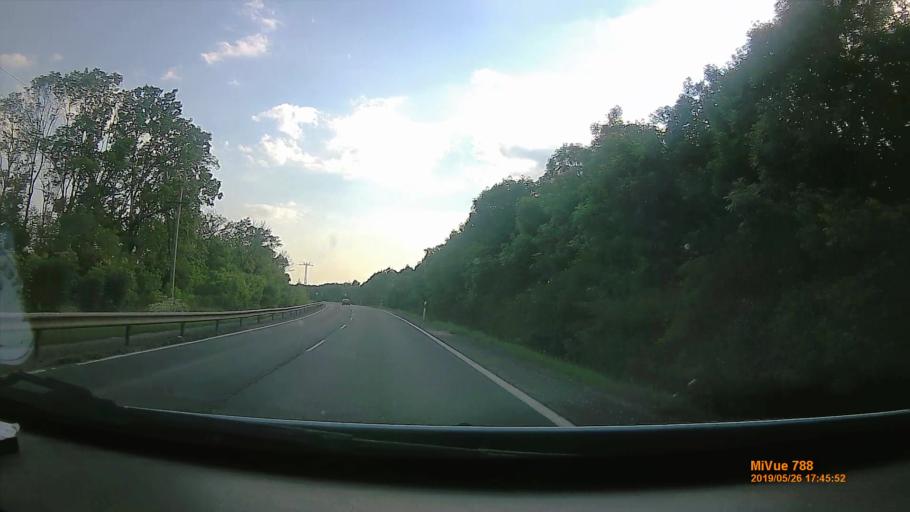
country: HU
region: Borsod-Abauj-Zemplen
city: Szikszo
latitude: 48.2136
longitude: 20.9440
